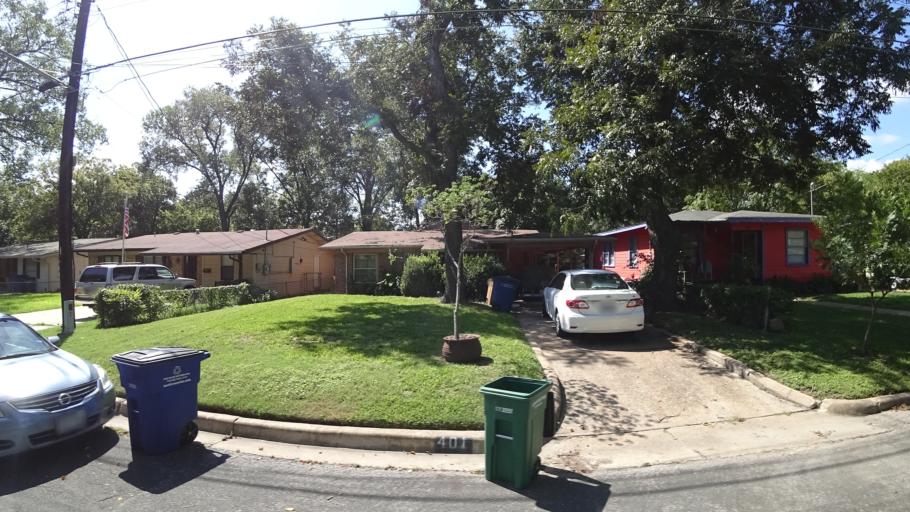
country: US
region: Texas
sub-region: Travis County
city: Austin
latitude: 30.3291
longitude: -97.7187
